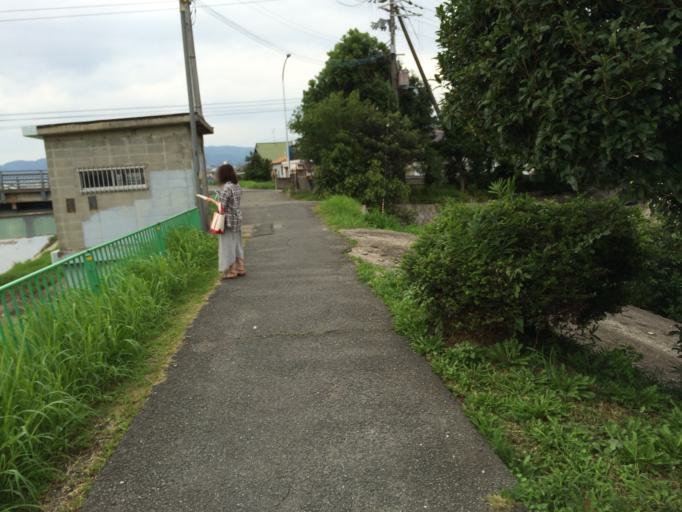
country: JP
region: Osaka
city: Ibaraki
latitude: 34.8228
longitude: 135.5807
